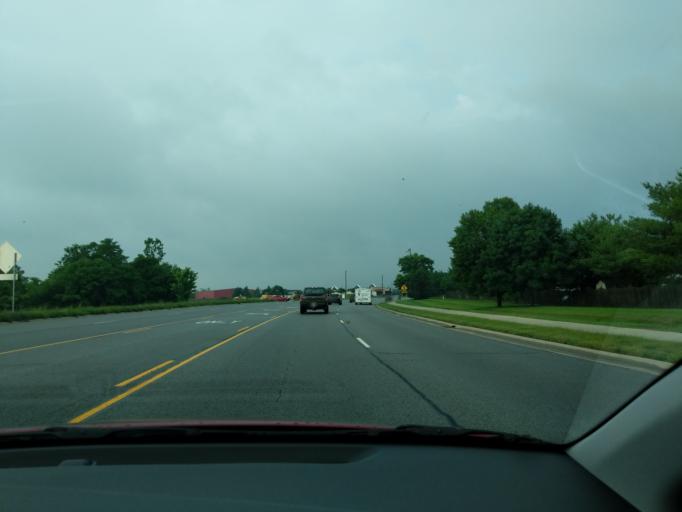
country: US
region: Indiana
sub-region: Hancock County
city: McCordsville
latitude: 39.8754
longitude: -85.9526
